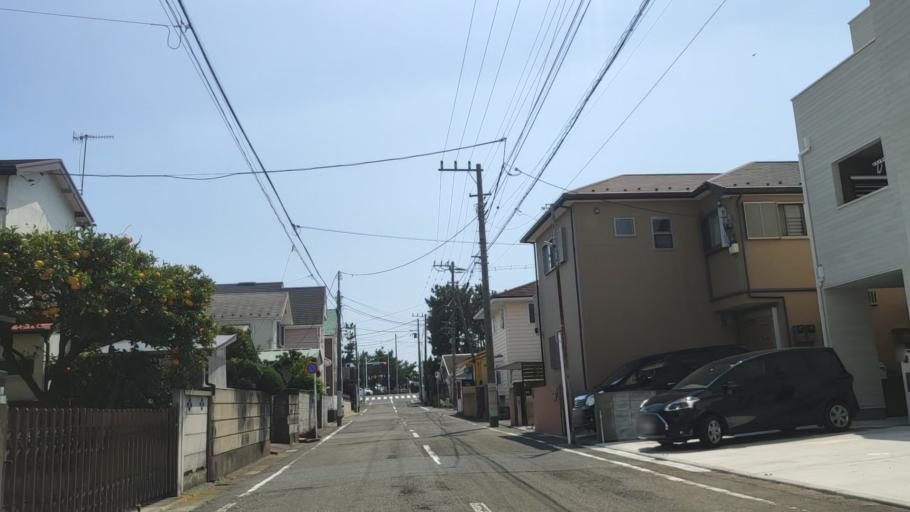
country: JP
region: Kanagawa
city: Hiratsuka
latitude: 35.3160
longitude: 139.3398
